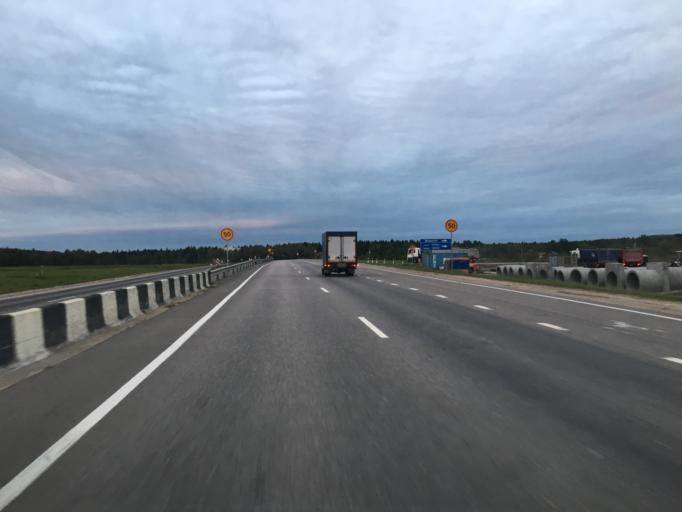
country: RU
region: Kaluga
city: Detchino
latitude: 54.6767
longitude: 36.2953
